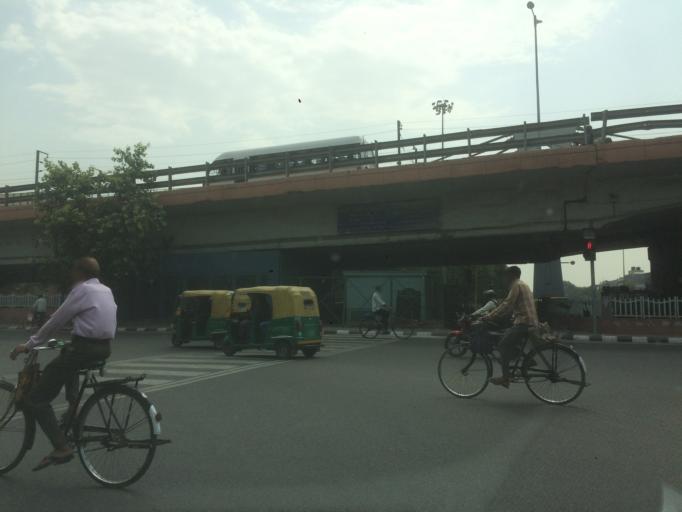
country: IN
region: NCT
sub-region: New Delhi
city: New Delhi
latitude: 28.5658
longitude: 77.2338
